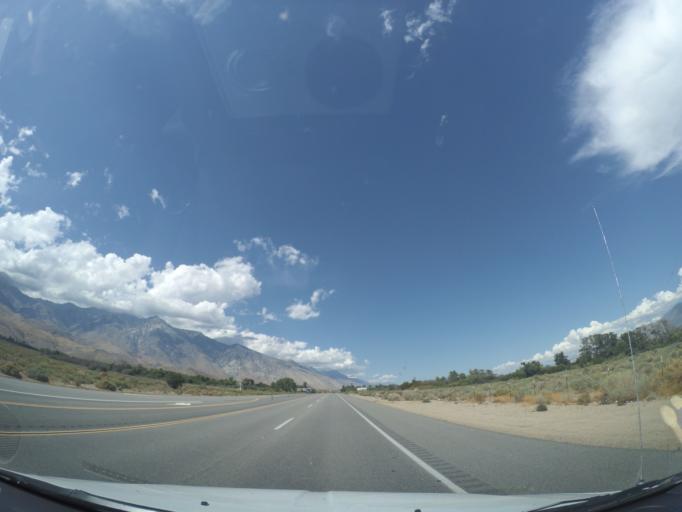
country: US
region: California
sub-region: Inyo County
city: Lone Pine
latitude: 36.8309
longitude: -118.2240
